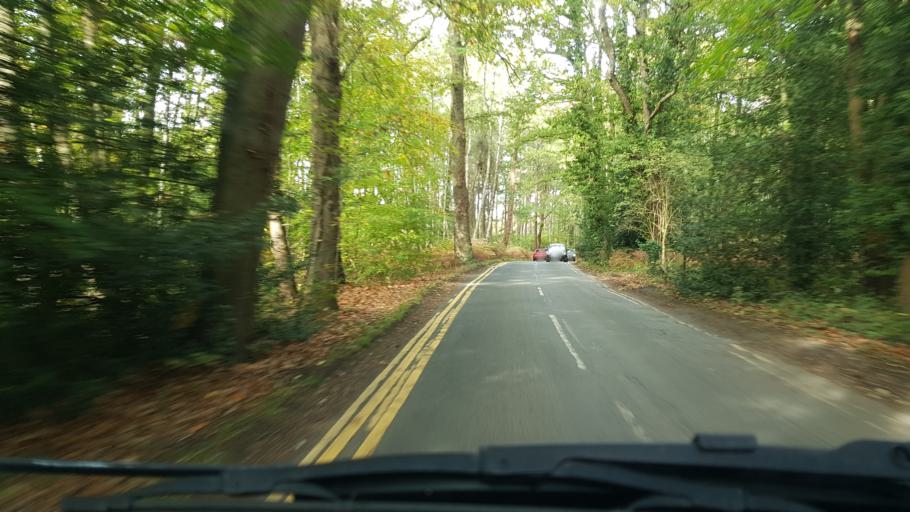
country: GB
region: England
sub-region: Surrey
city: Ripley
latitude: 51.3128
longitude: -0.4685
